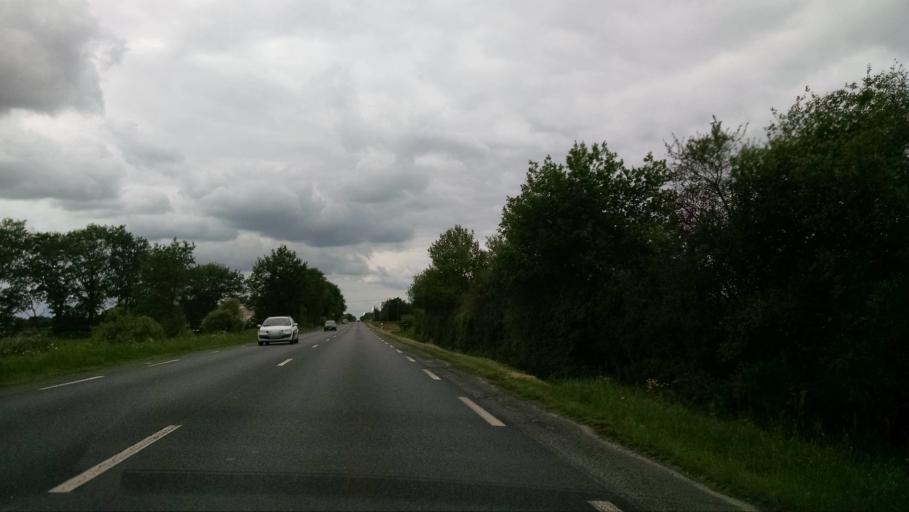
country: FR
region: Pays de la Loire
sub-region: Departement de la Loire-Atlantique
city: Aigrefeuille-sur-Maine
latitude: 47.0874
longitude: -1.4269
